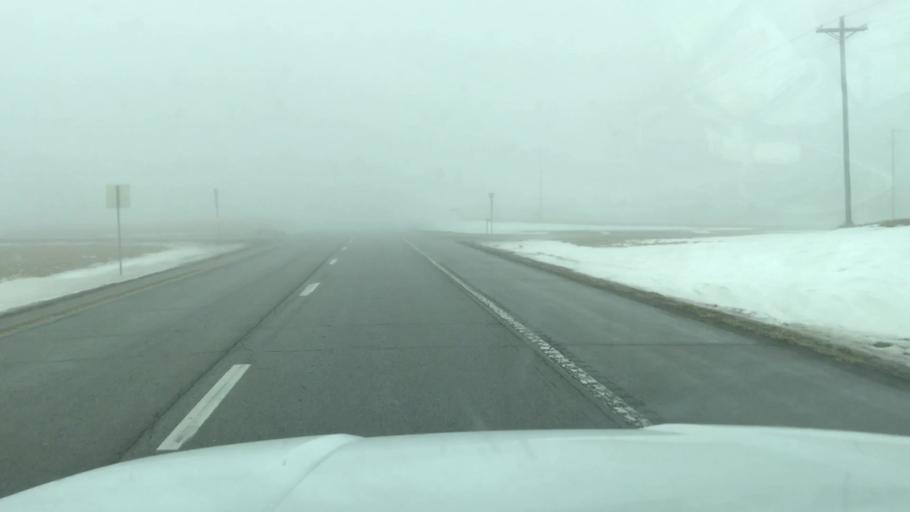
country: US
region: Missouri
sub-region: Clinton County
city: Cameron
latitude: 39.7549
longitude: -94.2995
